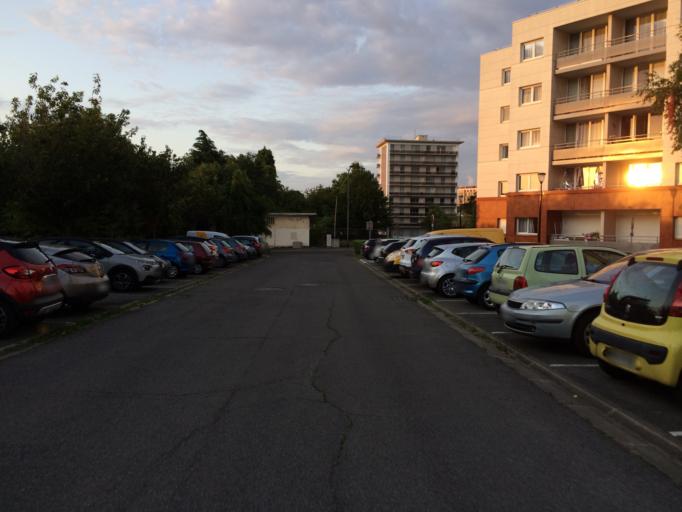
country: FR
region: Ile-de-France
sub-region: Departement des Hauts-de-Seine
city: Antony
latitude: 48.7487
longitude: 2.3104
